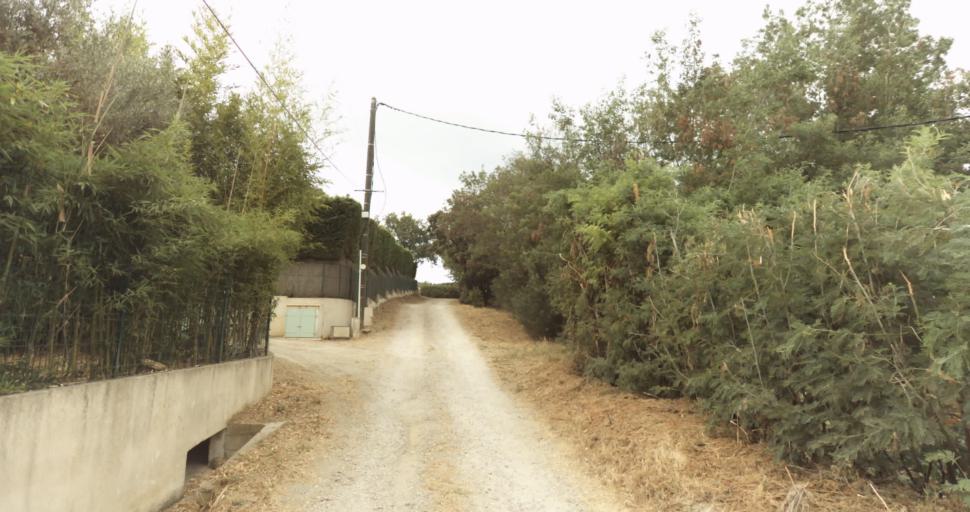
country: FR
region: Provence-Alpes-Cote d'Azur
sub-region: Departement du Var
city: La Croix-Valmer
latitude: 43.2131
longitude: 6.5761
